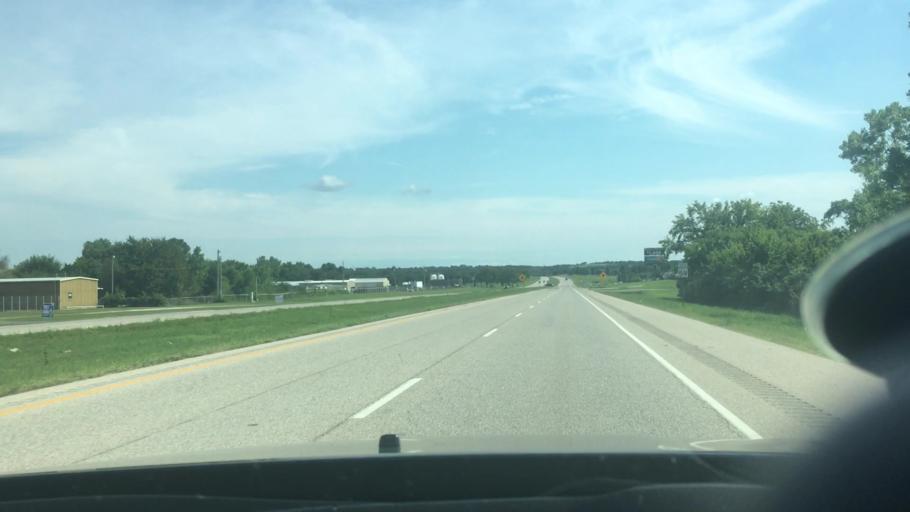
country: US
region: Oklahoma
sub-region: Seminole County
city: Seminole
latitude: 35.1934
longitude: -96.6752
